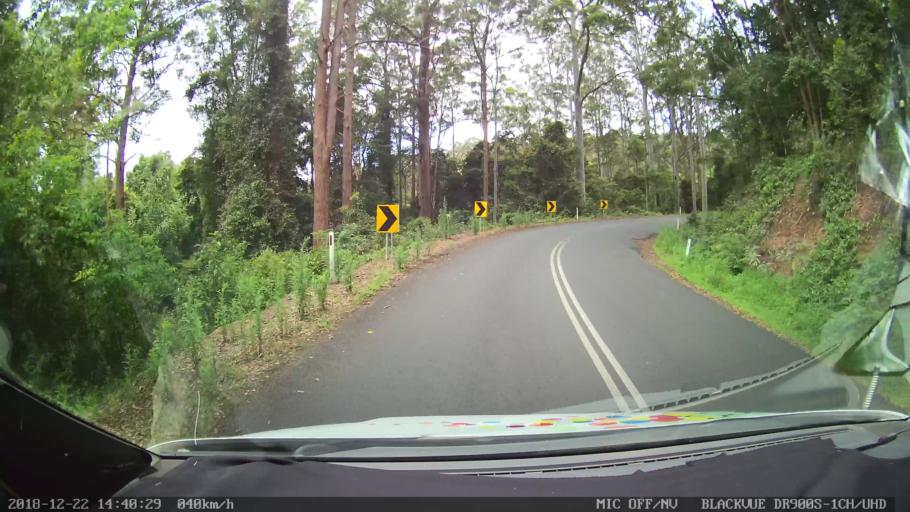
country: AU
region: New South Wales
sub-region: Bellingen
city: Dorrigo
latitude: -30.1508
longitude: 152.5884
